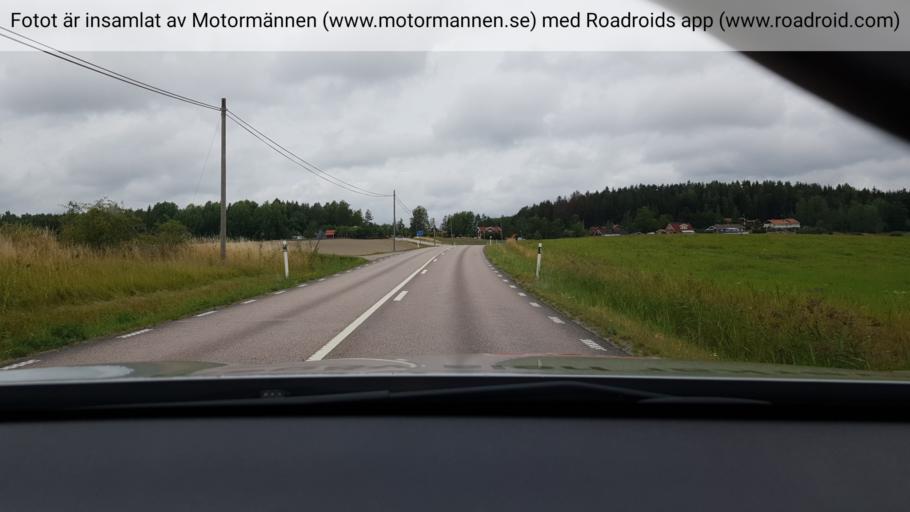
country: SE
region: Soedermanland
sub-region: Gnesta Kommun
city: Gnesta
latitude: 59.0604
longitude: 17.1752
